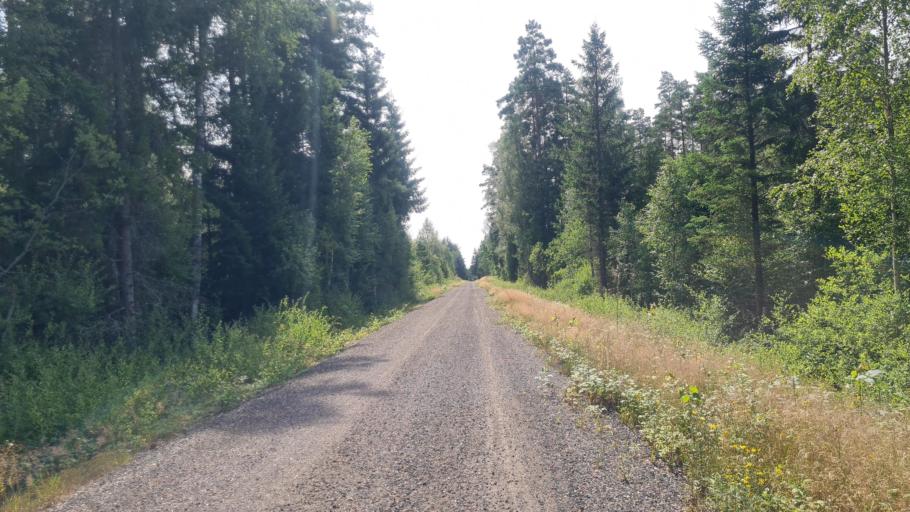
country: SE
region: Kronoberg
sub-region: Ljungby Kommun
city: Lagan
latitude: 56.9637
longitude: 13.9538
